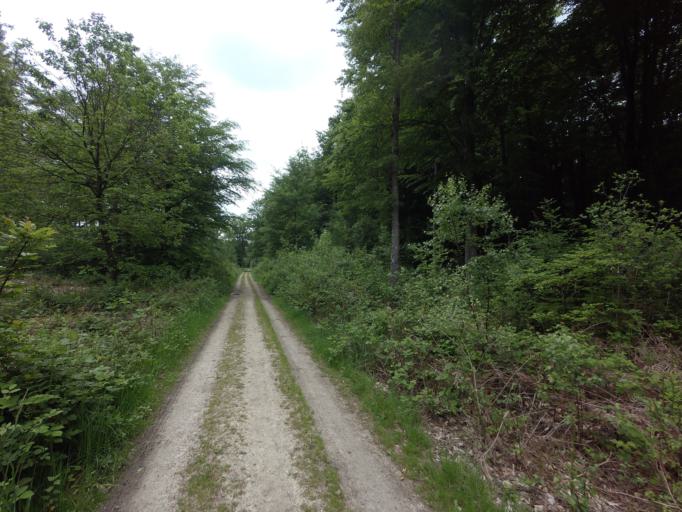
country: BE
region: Wallonia
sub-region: Province de Liege
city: Aubel
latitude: 50.7643
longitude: 5.8931
